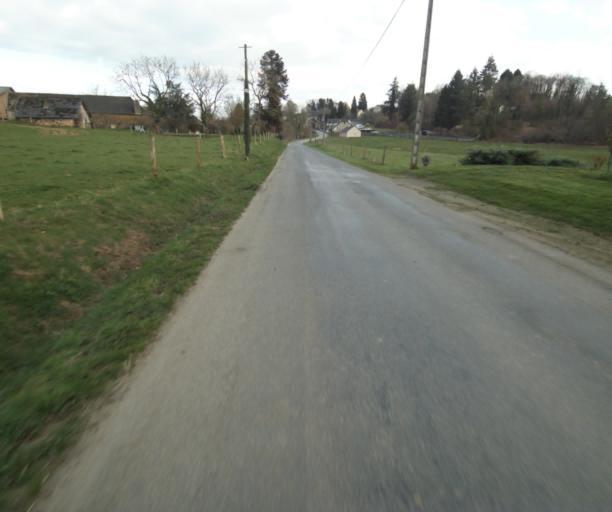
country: FR
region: Limousin
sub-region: Departement de la Correze
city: Saint-Clement
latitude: 45.3571
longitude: 1.6314
